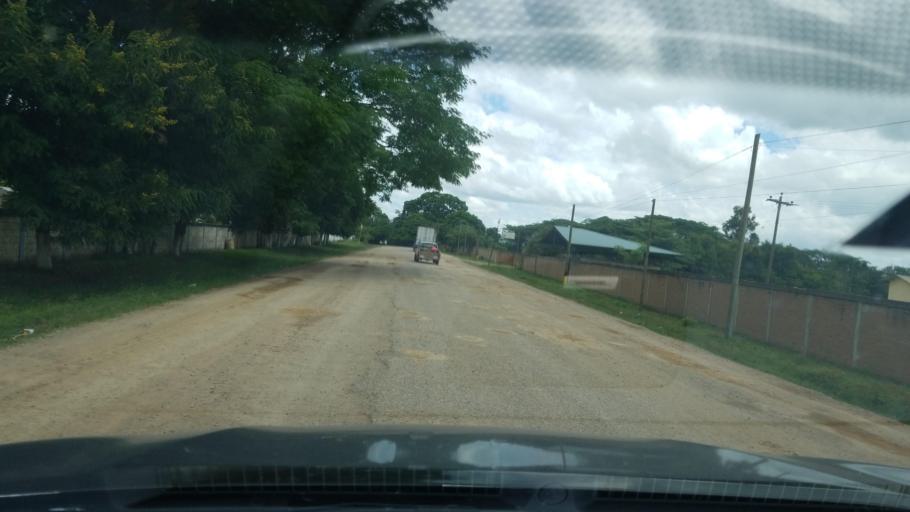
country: HN
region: Francisco Morazan
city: Talanga
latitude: 14.3951
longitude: -87.0780
